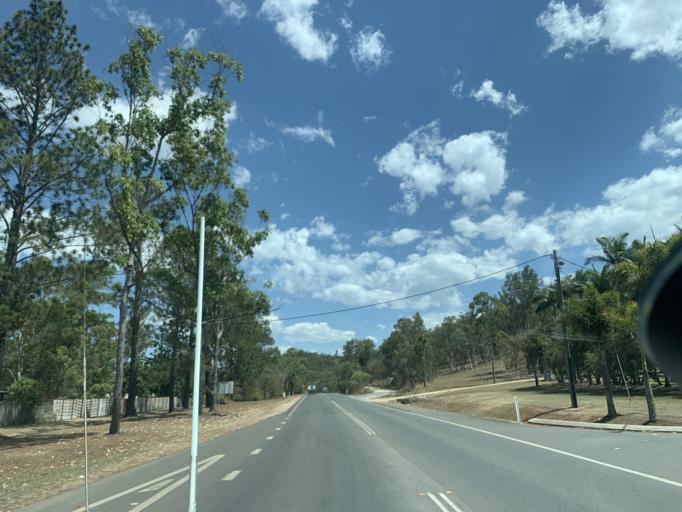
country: AU
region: Queensland
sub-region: Tablelands
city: Atherton
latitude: -17.2818
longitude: 145.4697
